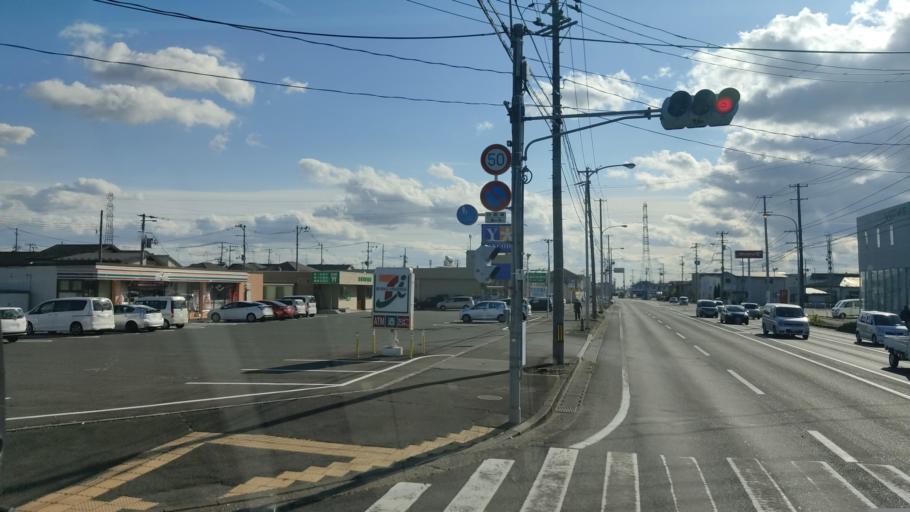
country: JP
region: Iwate
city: Morioka-shi
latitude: 39.6825
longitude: 141.1434
